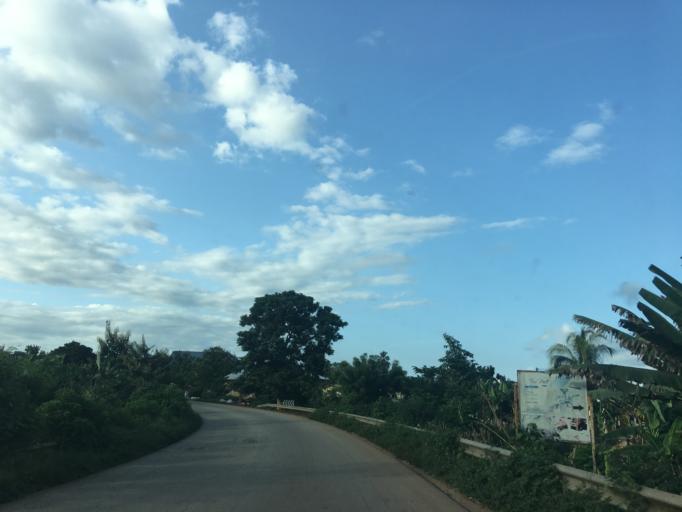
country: GH
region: Western
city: Bibiani
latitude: 6.3271
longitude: -2.2502
